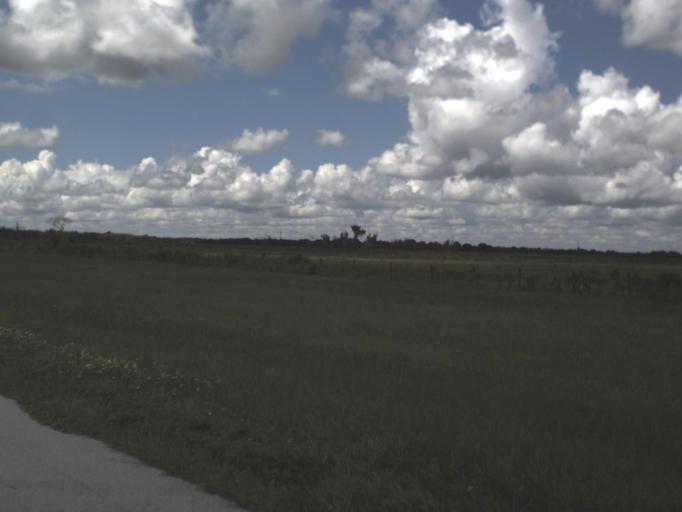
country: US
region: Florida
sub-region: DeSoto County
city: Southeast Arcadia
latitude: 27.2094
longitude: -81.7394
